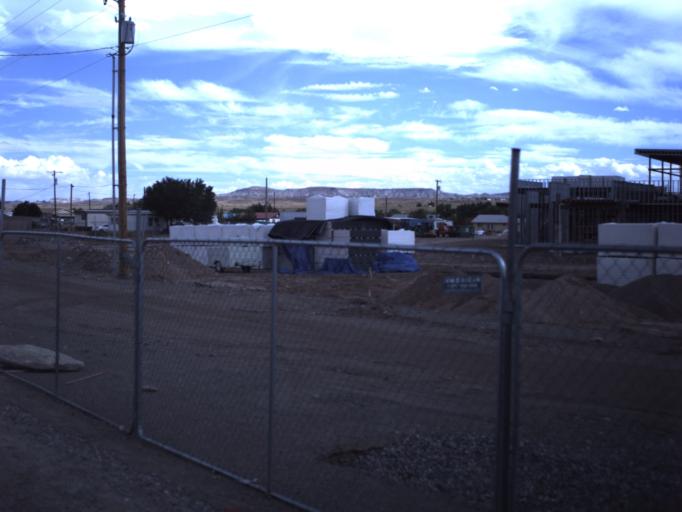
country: US
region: Utah
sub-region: San Juan County
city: Blanding
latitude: 37.2609
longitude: -109.3040
